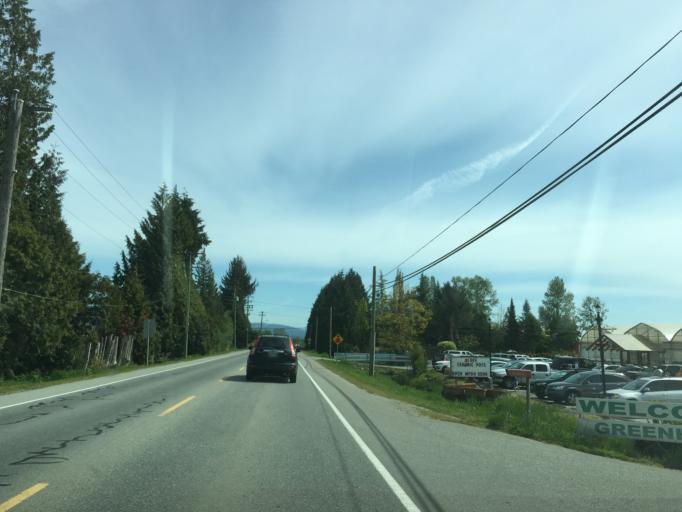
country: CA
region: British Columbia
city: Pitt Meadows
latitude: 49.2441
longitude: -122.6926
